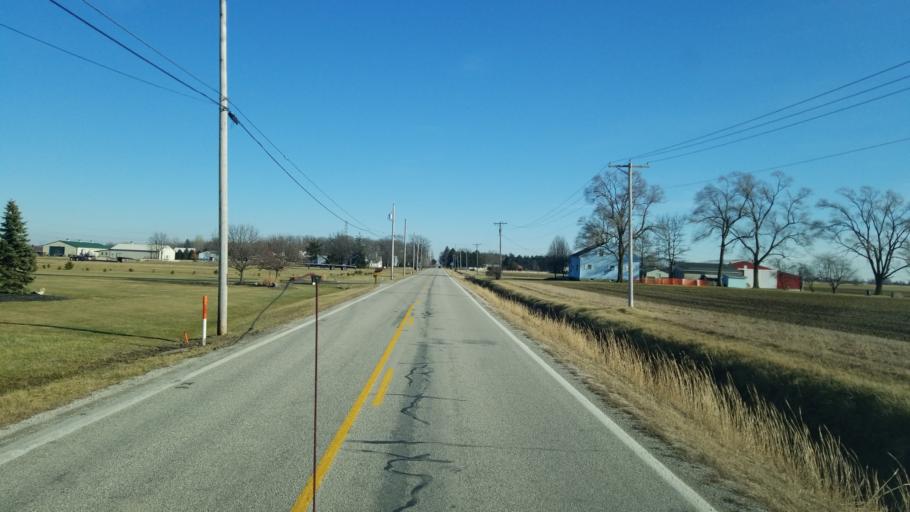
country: US
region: Ohio
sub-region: Wood County
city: Luckey
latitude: 41.4499
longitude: -83.4532
